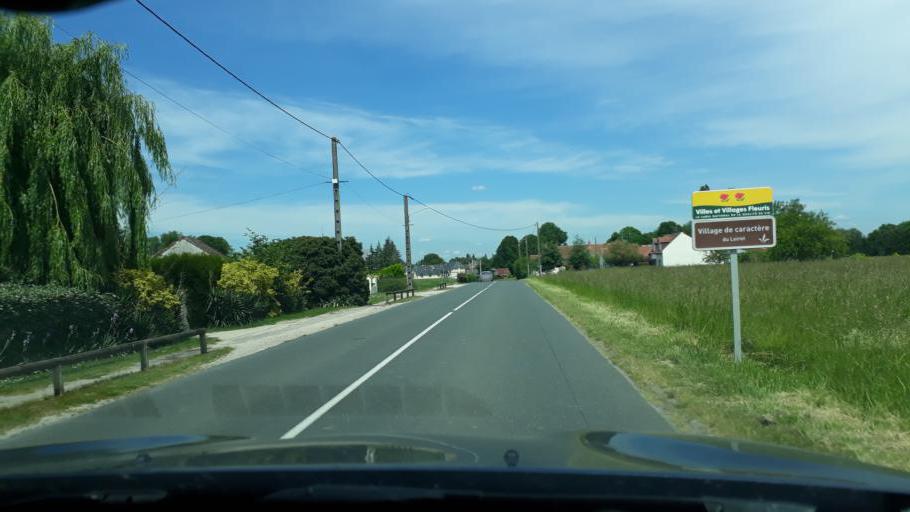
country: FR
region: Centre
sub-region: Departement du Loiret
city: Boiscommun
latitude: 48.0531
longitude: 2.2978
